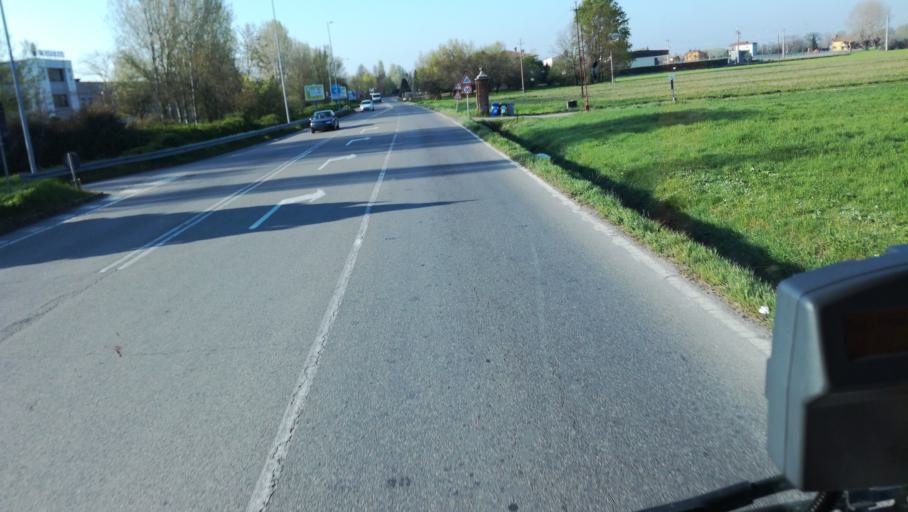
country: IT
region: Emilia-Romagna
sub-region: Provincia di Modena
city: Villanova
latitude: 44.6804
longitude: 10.9367
